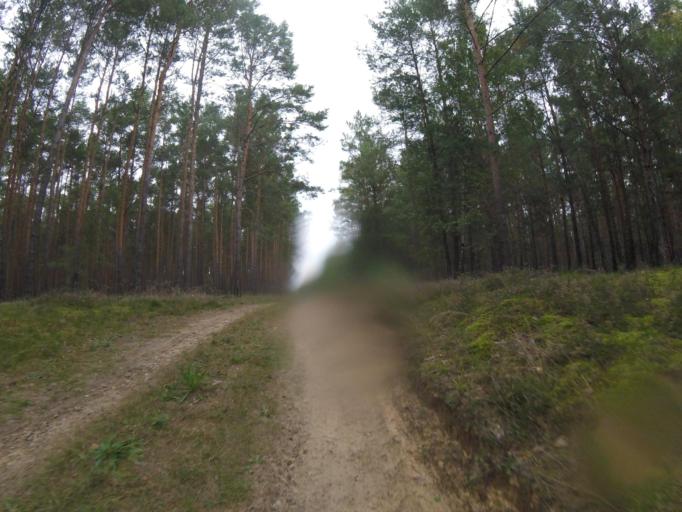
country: DE
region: Brandenburg
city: Gross Koris
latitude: 52.1865
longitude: 13.6756
